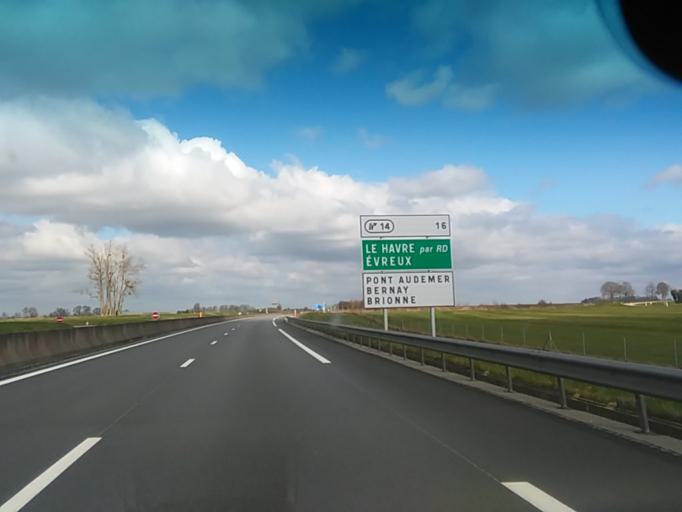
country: FR
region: Lower Normandy
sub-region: Departement du Calvados
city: Orbec
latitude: 49.0370
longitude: 0.4438
